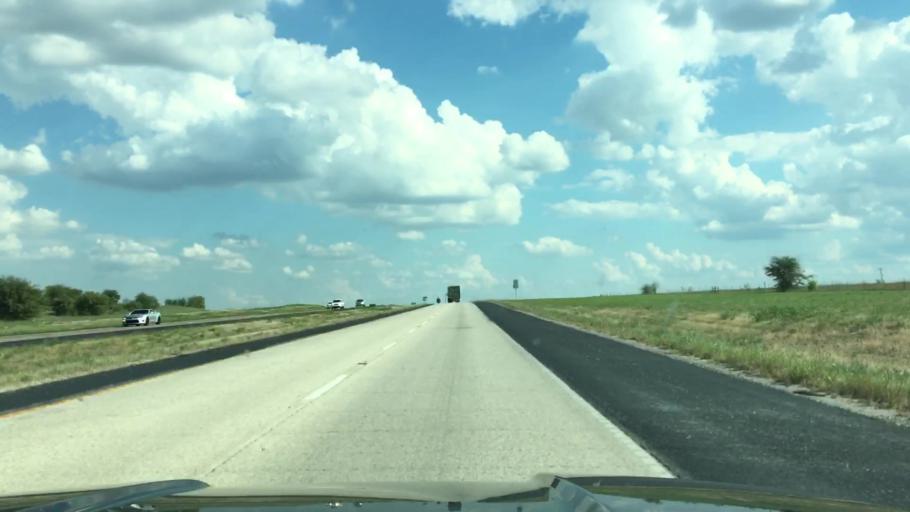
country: US
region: Texas
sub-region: Wise County
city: New Fairview
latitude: 33.1129
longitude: -97.4791
